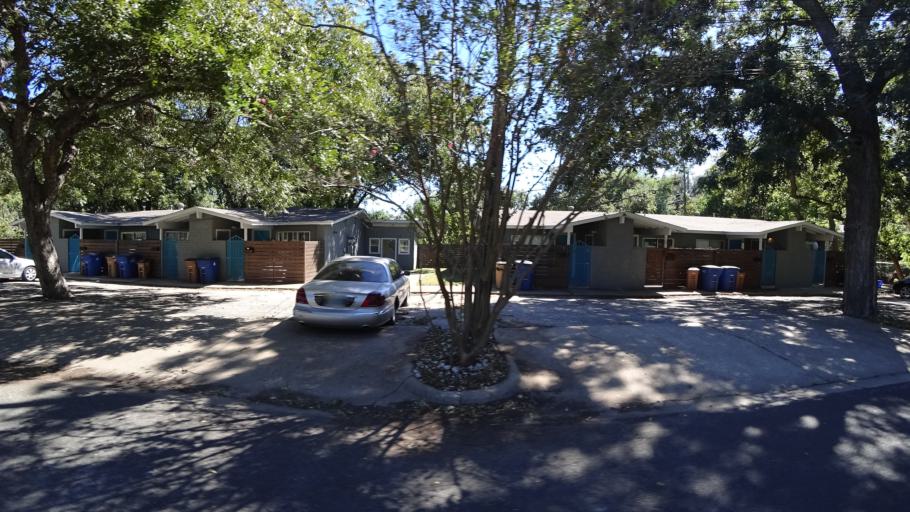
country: US
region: Texas
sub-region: Travis County
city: Austin
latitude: 30.2397
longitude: -97.7404
